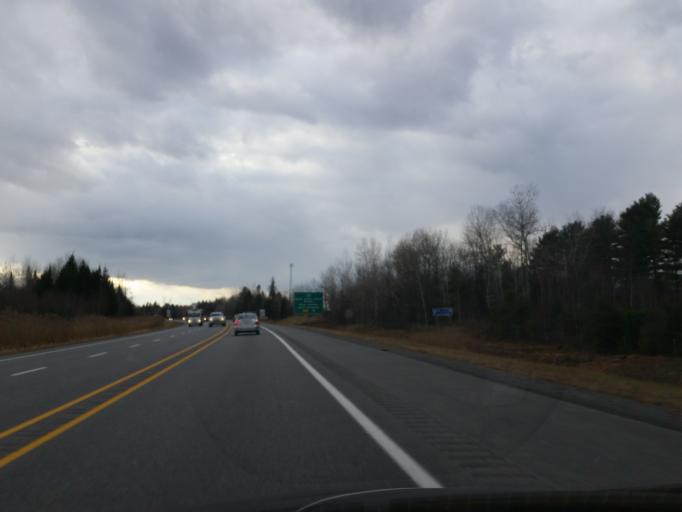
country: CA
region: Quebec
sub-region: Laurentides
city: Saint-Colomban
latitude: 45.6789
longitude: -74.1721
